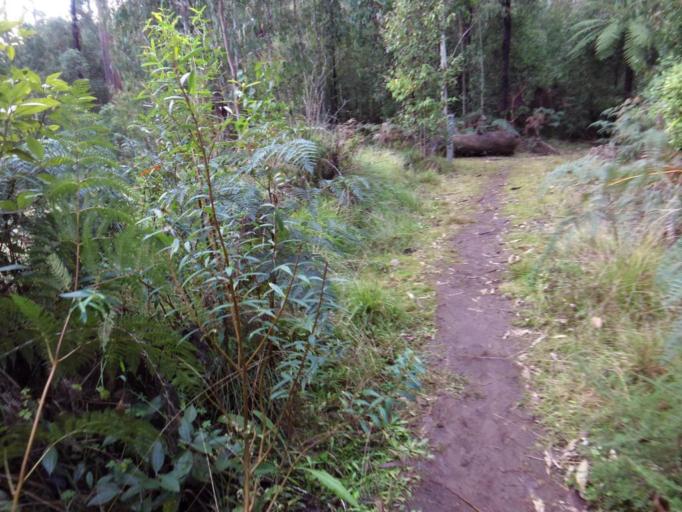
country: AU
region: Victoria
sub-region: Yarra Ranges
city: Millgrove
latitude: -37.5315
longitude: 145.7513
